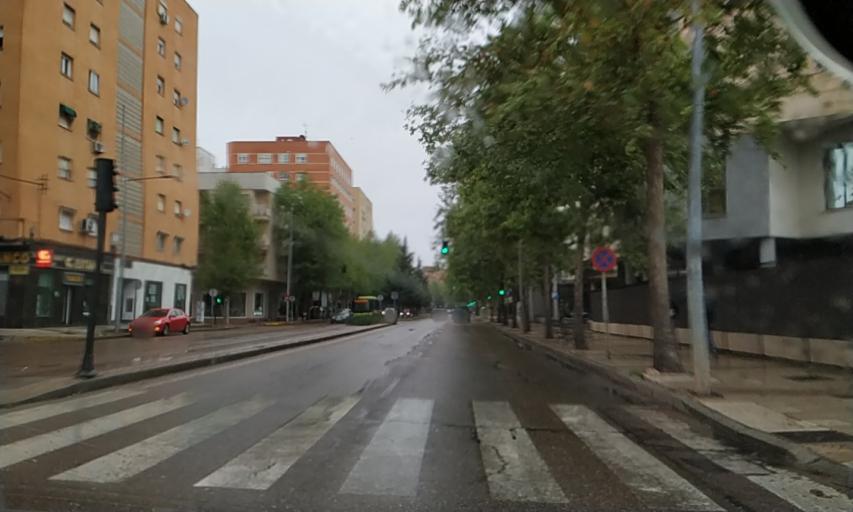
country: ES
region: Extremadura
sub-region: Provincia de Badajoz
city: Badajoz
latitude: 38.8656
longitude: -6.9728
